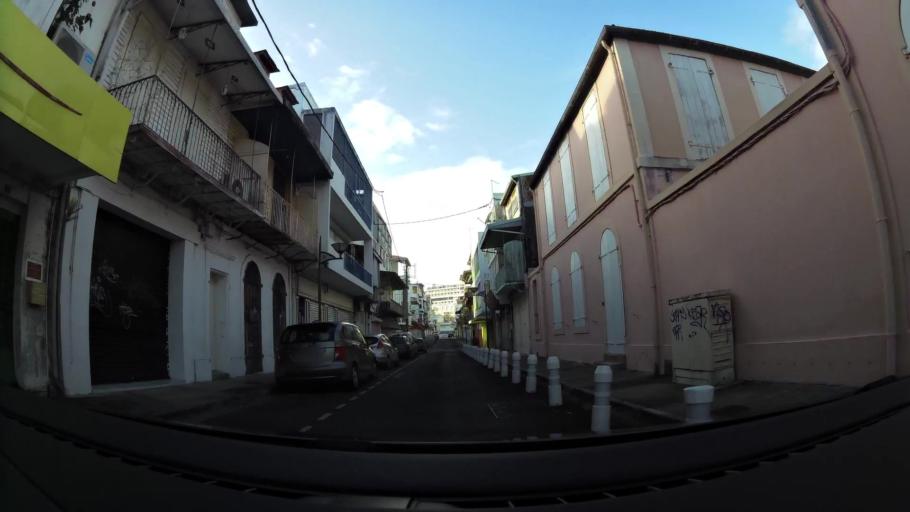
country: GP
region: Guadeloupe
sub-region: Guadeloupe
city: Pointe-a-Pitre
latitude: 16.2381
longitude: -61.5373
